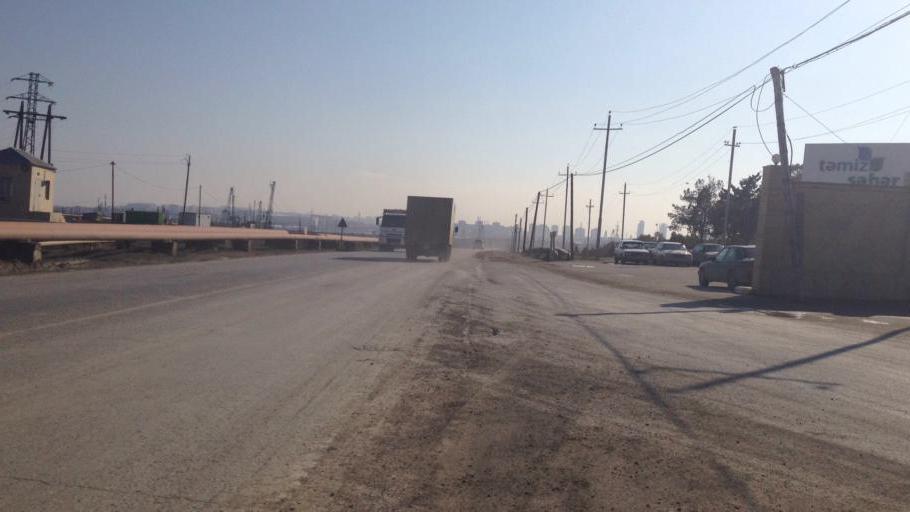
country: AZ
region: Baki
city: Balakhani
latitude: 40.4624
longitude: 49.8892
